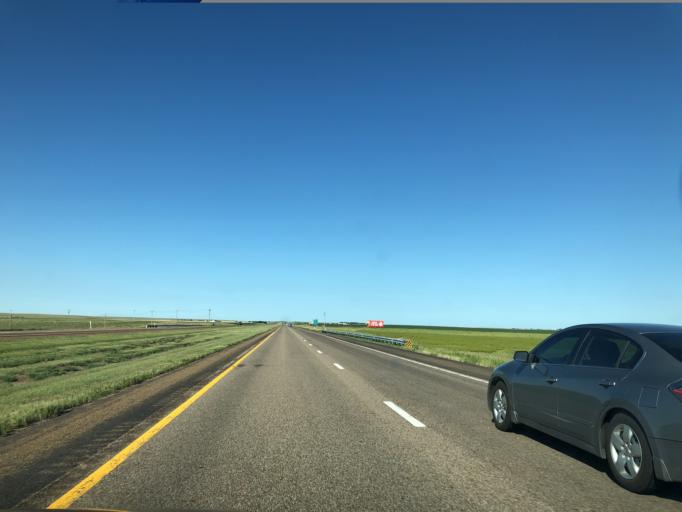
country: US
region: Kansas
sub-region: Thomas County
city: Colby
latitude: 39.3508
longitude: -101.3488
